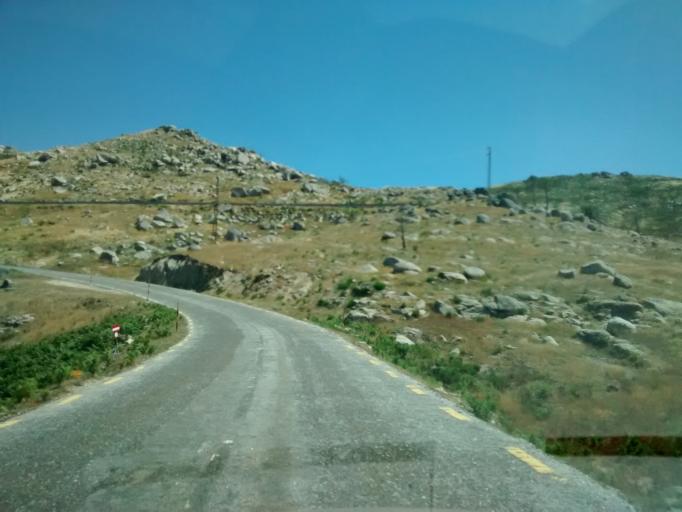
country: PT
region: Guarda
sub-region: Manteigas
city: Manteigas
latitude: 40.4225
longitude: -7.6187
